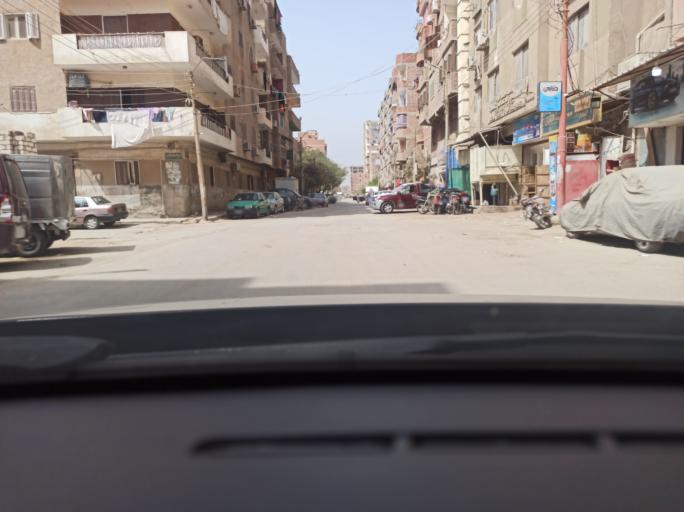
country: EG
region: Muhafazat Bani Suwayf
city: Bani Suwayf
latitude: 29.0825
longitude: 31.0911
